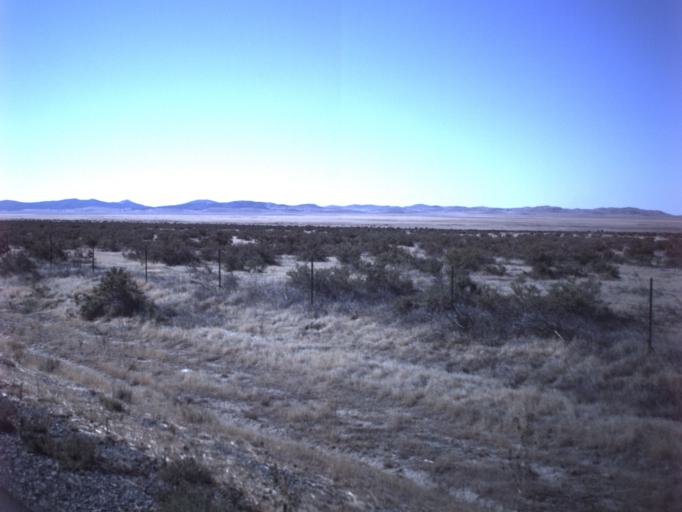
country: US
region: Utah
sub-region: Tooele County
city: Grantsville
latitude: 40.3589
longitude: -112.7458
